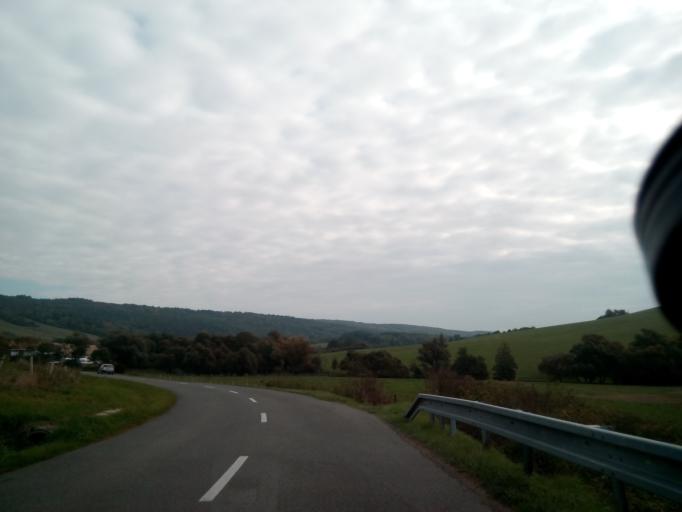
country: SK
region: Presovsky
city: Svidnik
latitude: 49.2470
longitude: 21.4441
